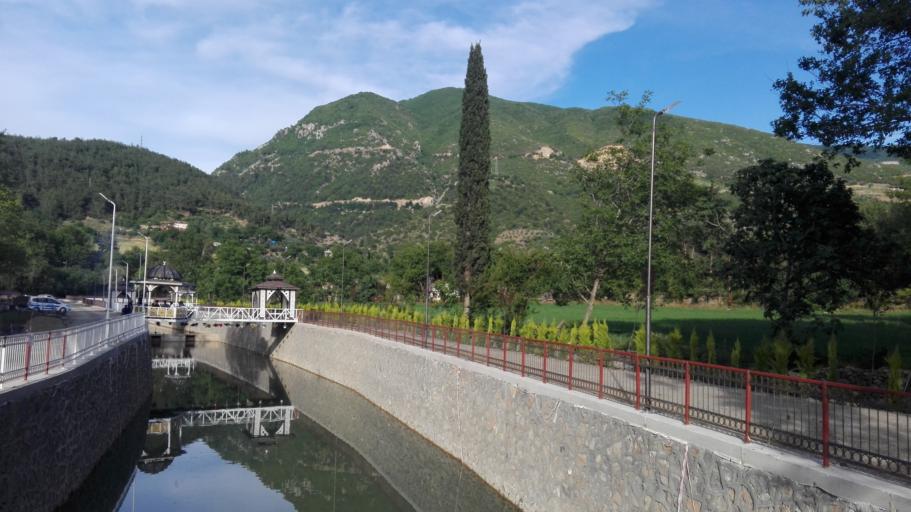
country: TR
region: Osmaniye
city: Haruniye
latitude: 37.2806
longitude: 36.4642
